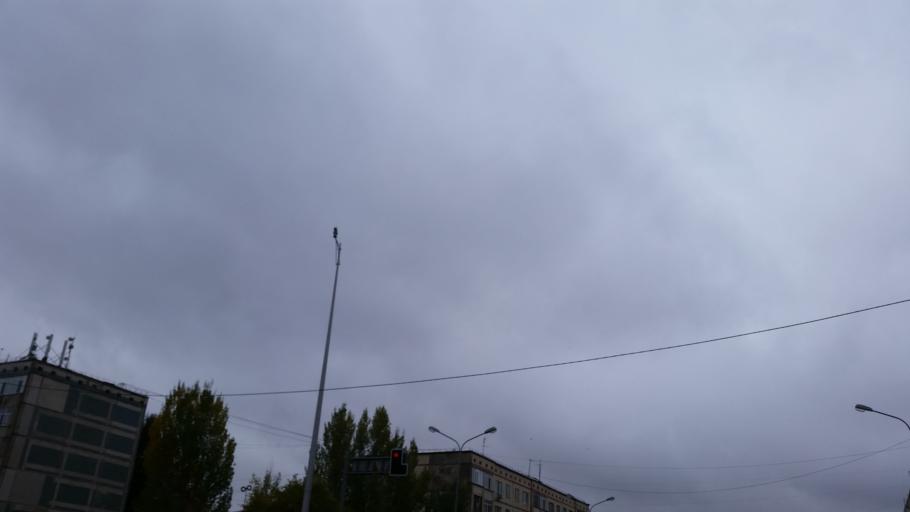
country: KZ
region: Astana Qalasy
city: Astana
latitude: 51.1551
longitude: 71.5031
